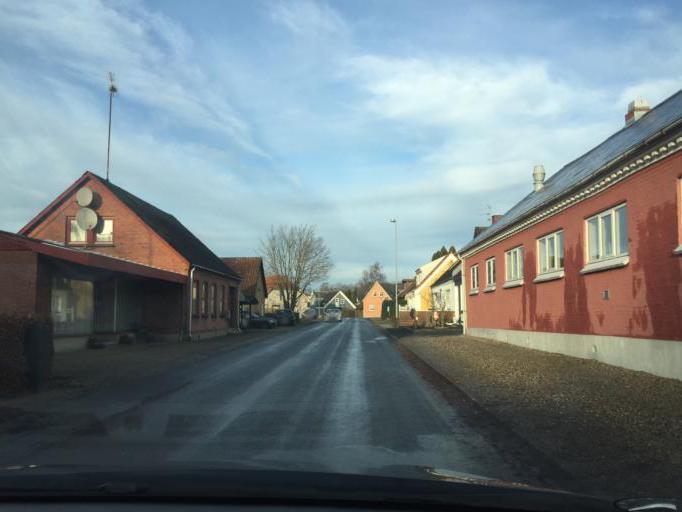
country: DK
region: South Denmark
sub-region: Faaborg-Midtfyn Kommune
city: Ringe
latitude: 55.2001
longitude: 10.4105
